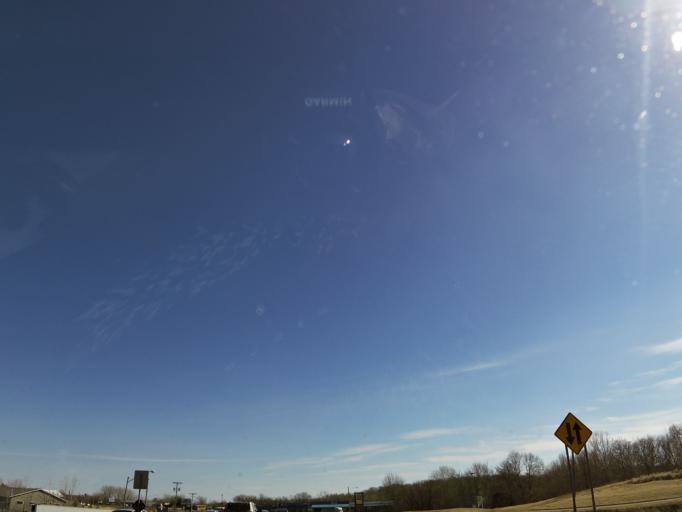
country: US
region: Minnesota
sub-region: Wright County
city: Rockford
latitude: 45.0820
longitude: -93.7294
